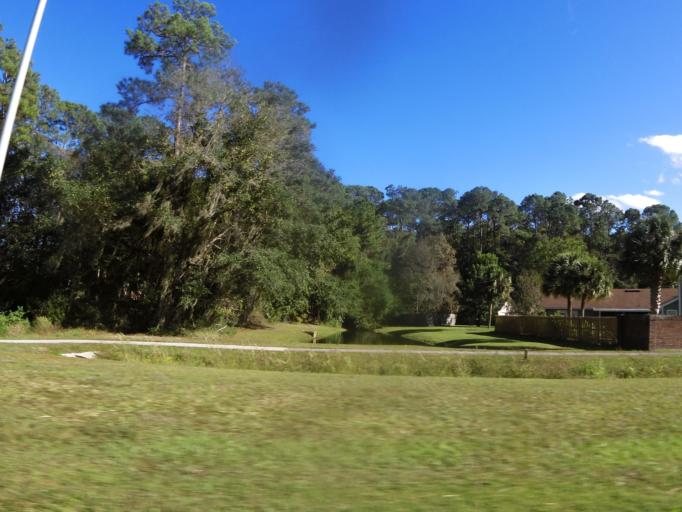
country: US
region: Florida
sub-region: Alachua County
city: Alachua
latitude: 29.7136
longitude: -82.3865
